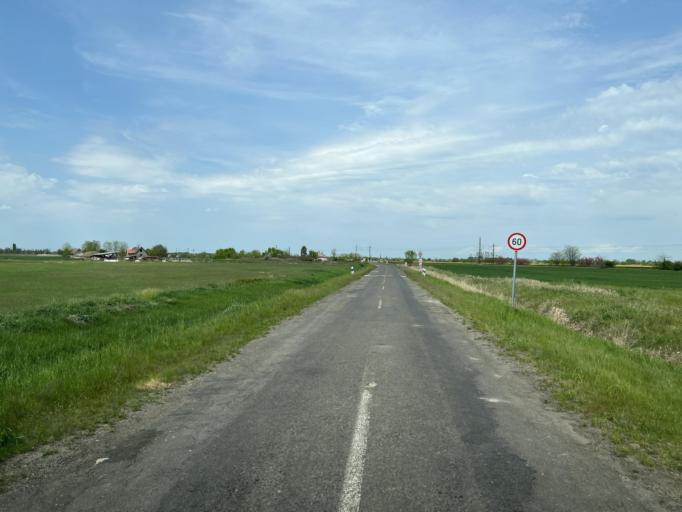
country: HU
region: Pest
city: Tapiogyorgye
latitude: 47.3173
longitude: 19.9698
